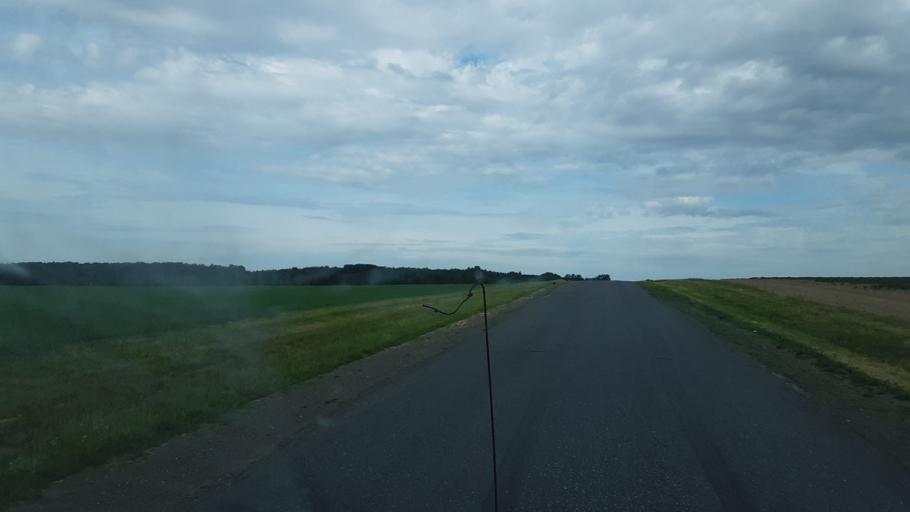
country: US
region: Maine
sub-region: Aroostook County
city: Caribou
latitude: 46.8116
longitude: -67.9994
